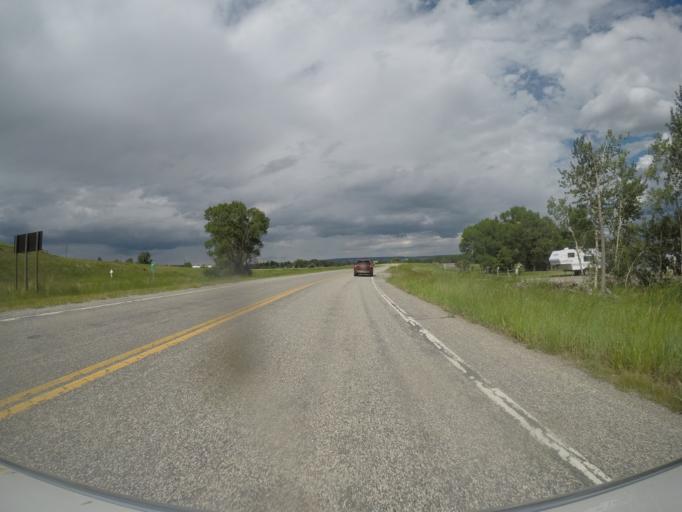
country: US
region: Montana
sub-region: Sweet Grass County
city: Big Timber
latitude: 45.8238
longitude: -109.9522
